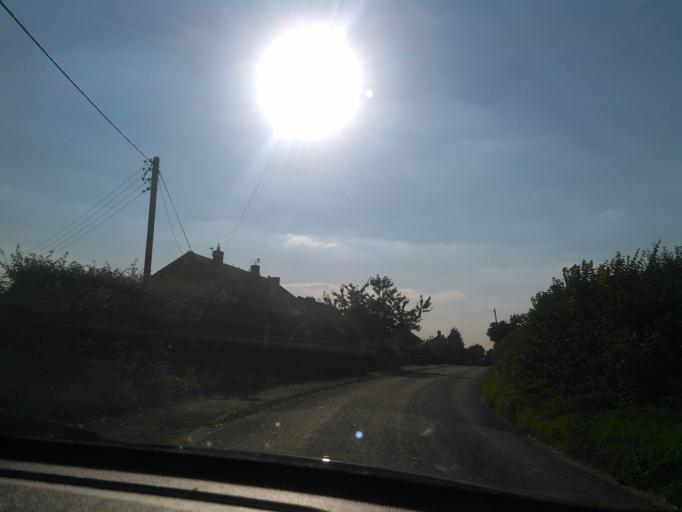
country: GB
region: England
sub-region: Telford and Wrekin
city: Eyton upon the Weald Moors
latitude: 52.7471
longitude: -2.4895
